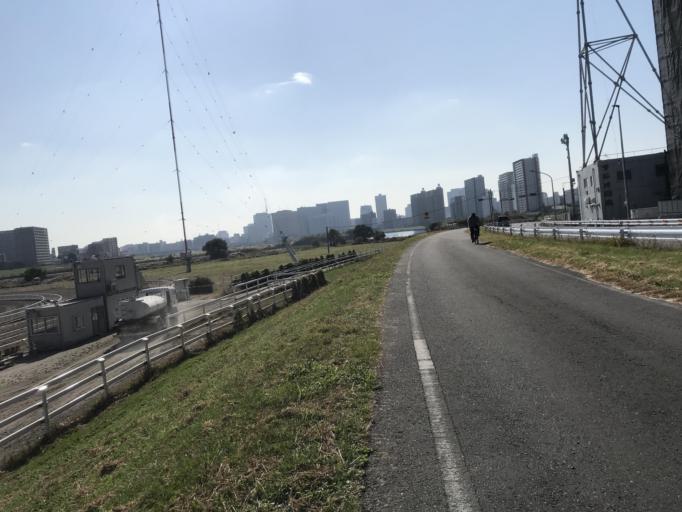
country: JP
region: Kanagawa
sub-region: Kawasaki-shi
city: Kawasaki
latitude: 35.5503
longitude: 139.6991
